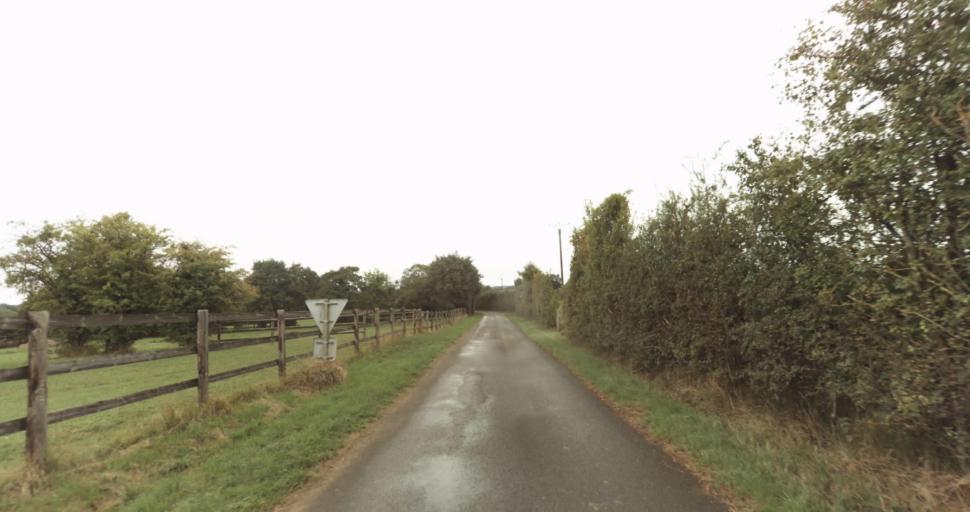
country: FR
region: Lower Normandy
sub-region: Departement de l'Orne
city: Sainte-Gauburge-Sainte-Colombe
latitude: 48.7307
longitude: 0.3676
